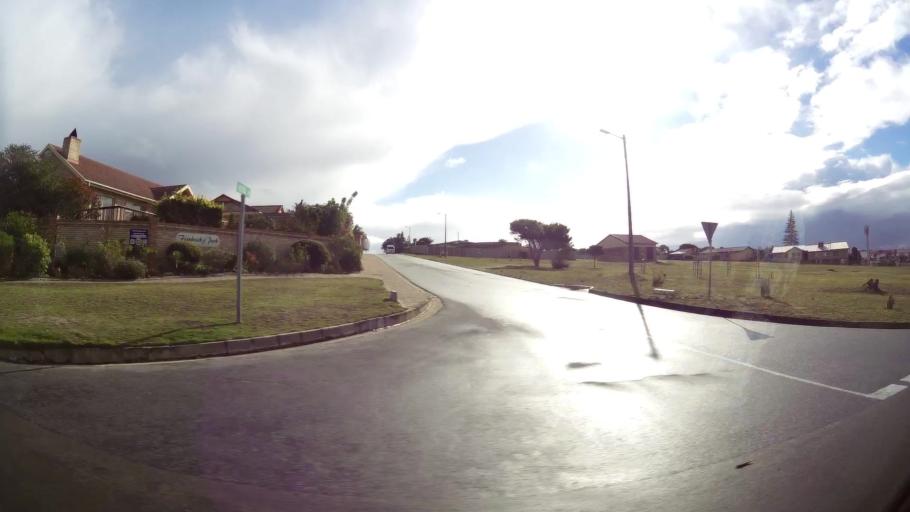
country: ZA
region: Western Cape
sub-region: Eden District Municipality
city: Mossel Bay
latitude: -34.1865
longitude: 22.1325
